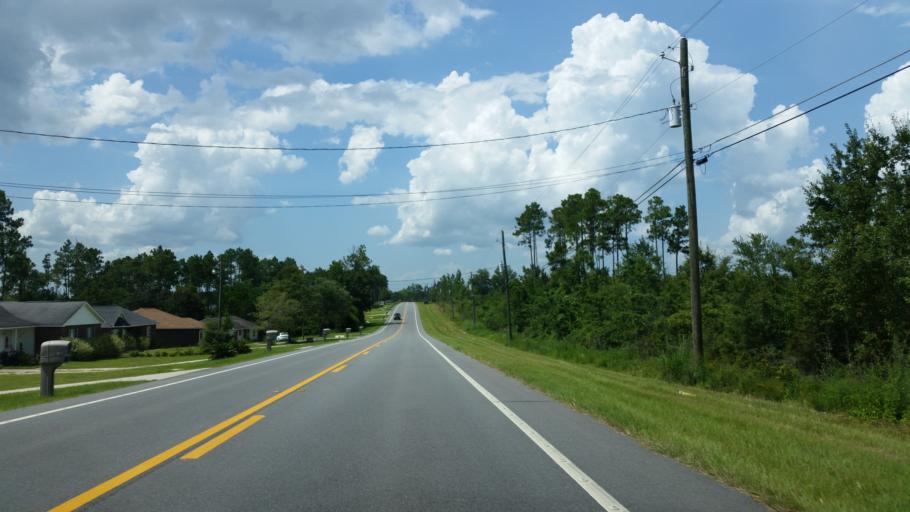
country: US
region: Florida
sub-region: Escambia County
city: Cantonment
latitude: 30.6246
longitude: -87.3753
